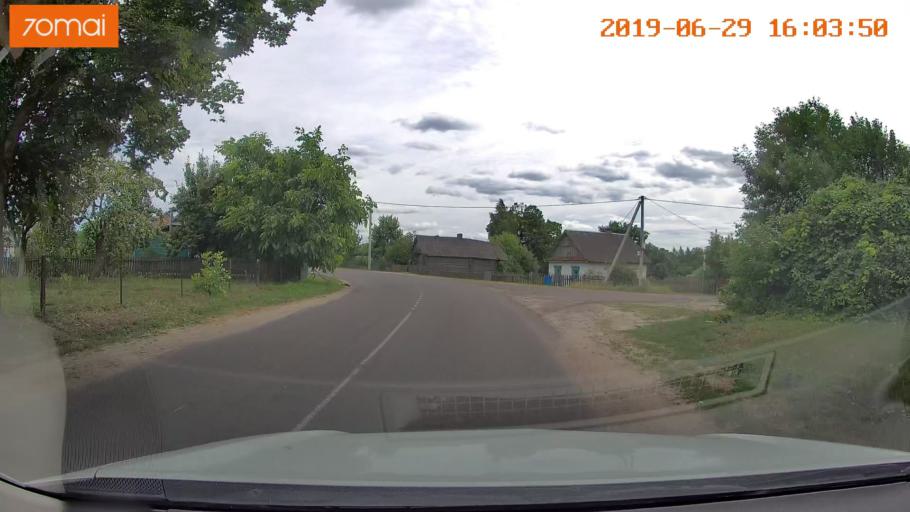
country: BY
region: Brest
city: Luninyets
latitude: 52.2273
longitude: 27.0216
